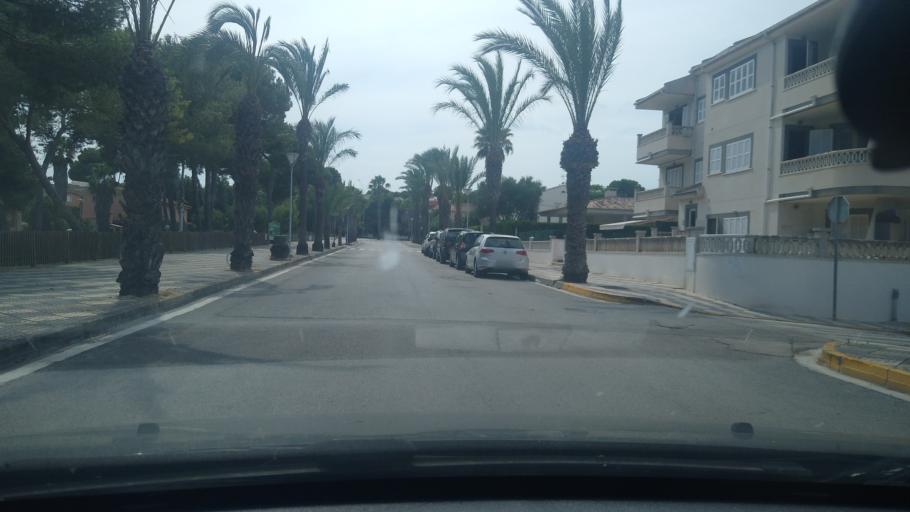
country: ES
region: Balearic Islands
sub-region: Illes Balears
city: Santa Margalida
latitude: 39.7595
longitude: 3.1614
